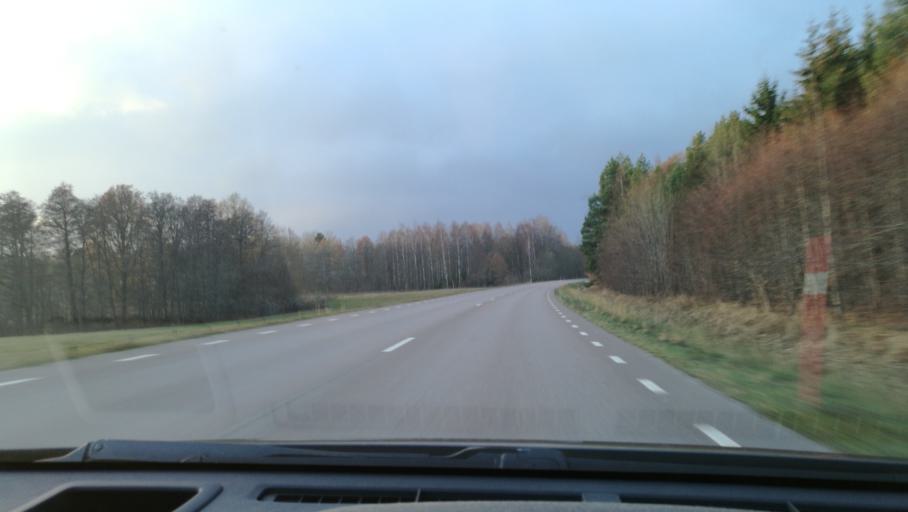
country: SE
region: Soedermanland
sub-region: Vingakers Kommun
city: Vingaker
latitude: 59.1637
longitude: 15.9923
